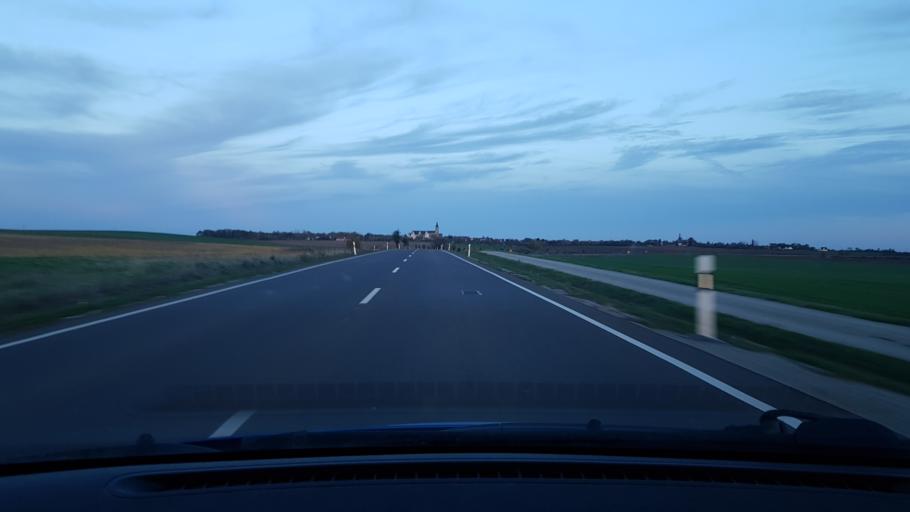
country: DE
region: Saxony-Anhalt
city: Leitzkau
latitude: 52.0598
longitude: 11.9226
